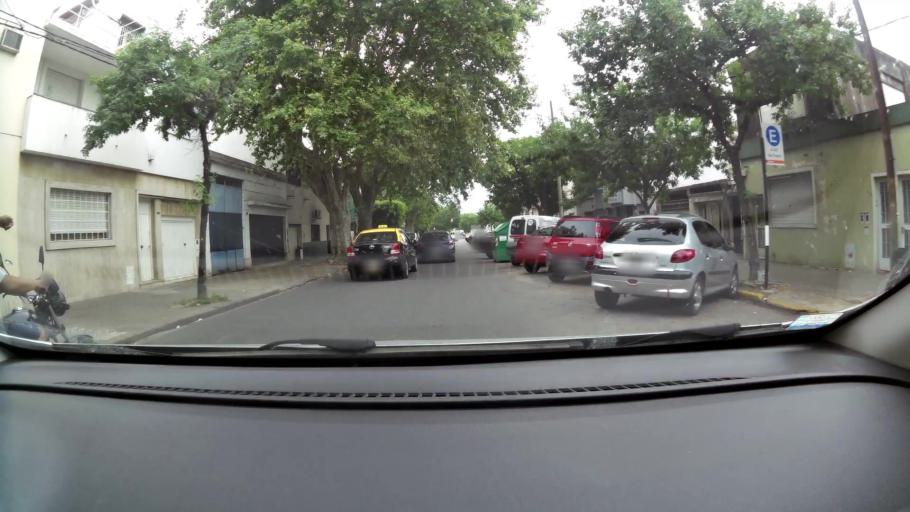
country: AR
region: Santa Fe
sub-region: Departamento de Rosario
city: Rosario
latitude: -32.9152
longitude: -60.6844
